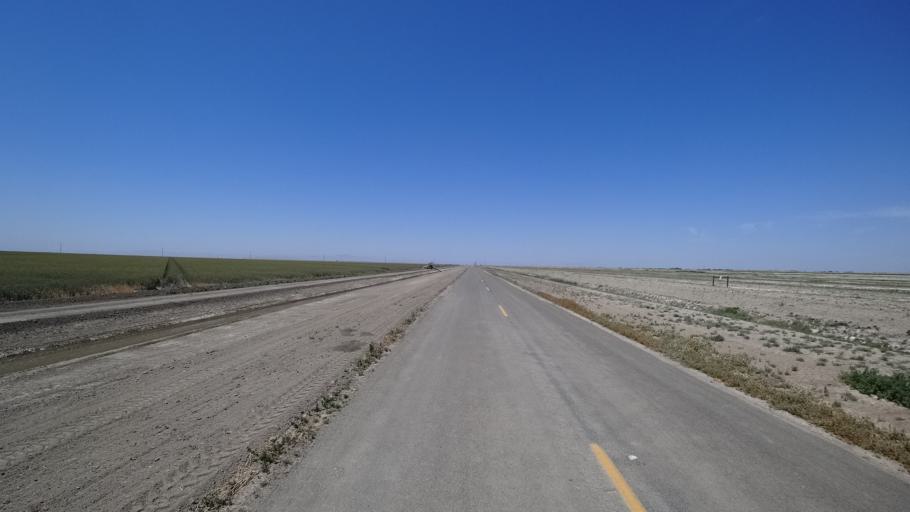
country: US
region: California
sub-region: Kings County
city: Corcoran
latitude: 36.1233
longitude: -119.6892
